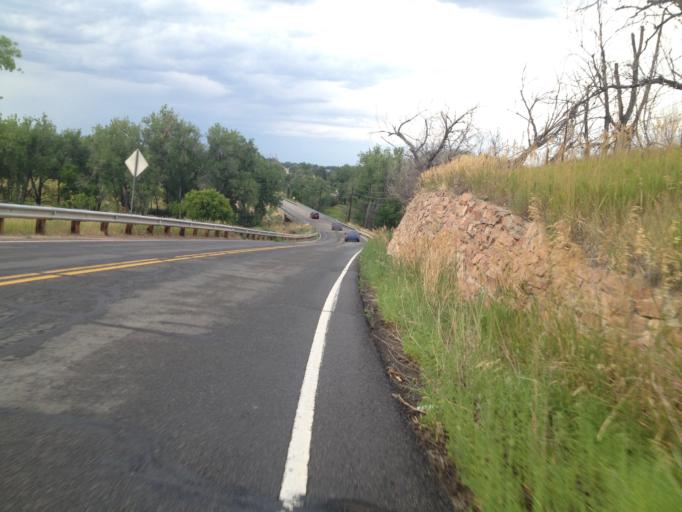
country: US
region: Colorado
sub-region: Boulder County
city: Louisville
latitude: 39.9674
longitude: -105.1283
